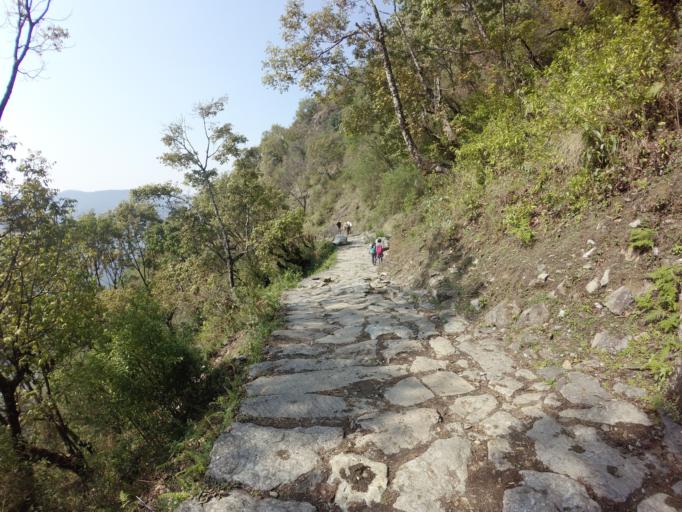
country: NP
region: Western Region
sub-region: Dhawalagiri Zone
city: Chitre
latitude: 28.3717
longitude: 83.8098
